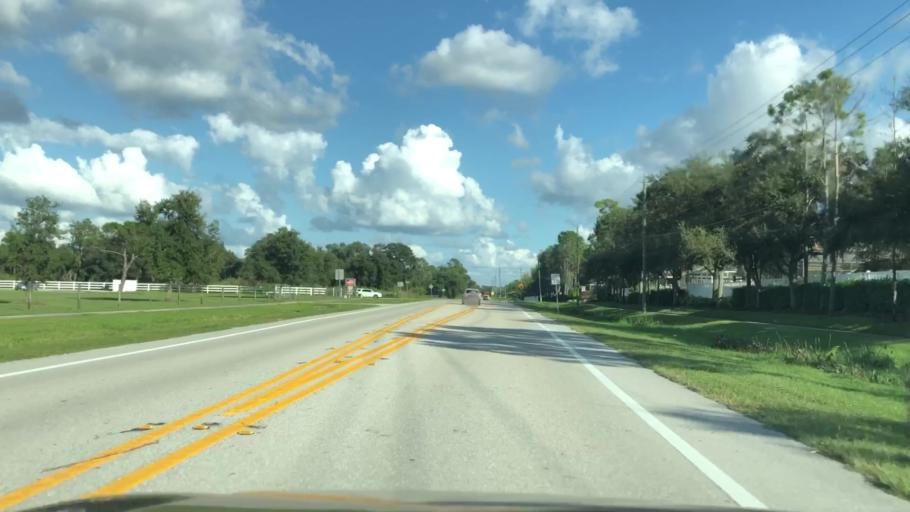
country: US
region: Florida
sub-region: Sarasota County
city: Fruitville
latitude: 27.3246
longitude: -82.4263
